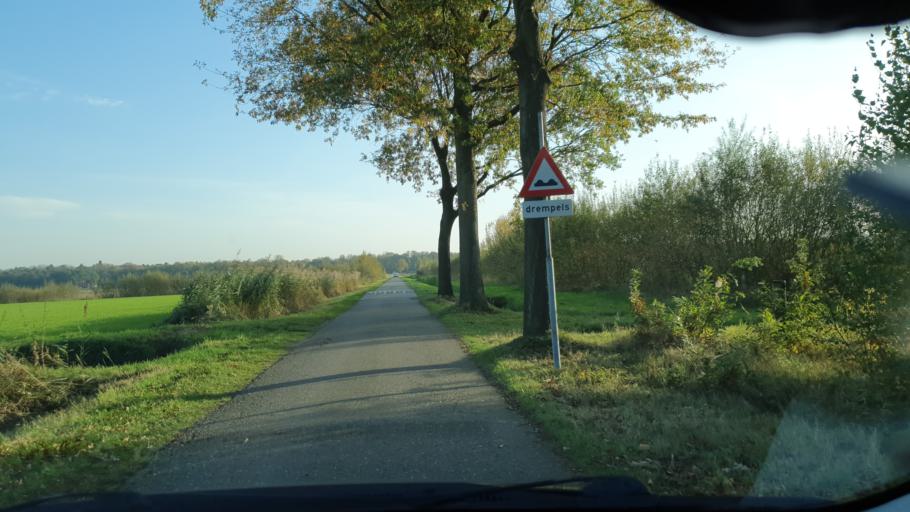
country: NL
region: Limburg
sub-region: Gemeente Roerdalen
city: Montfort
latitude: 51.1303
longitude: 5.9214
